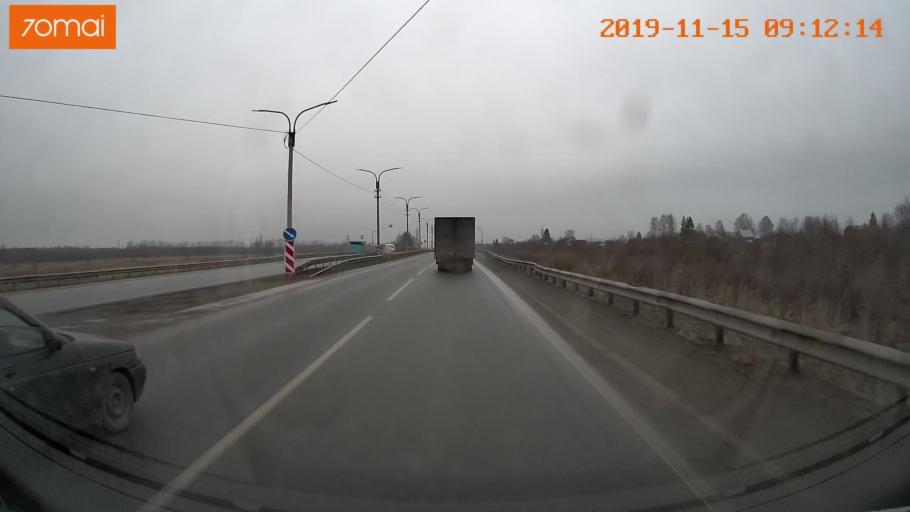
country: RU
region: Vologda
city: Tonshalovo
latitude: 59.2058
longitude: 37.9393
